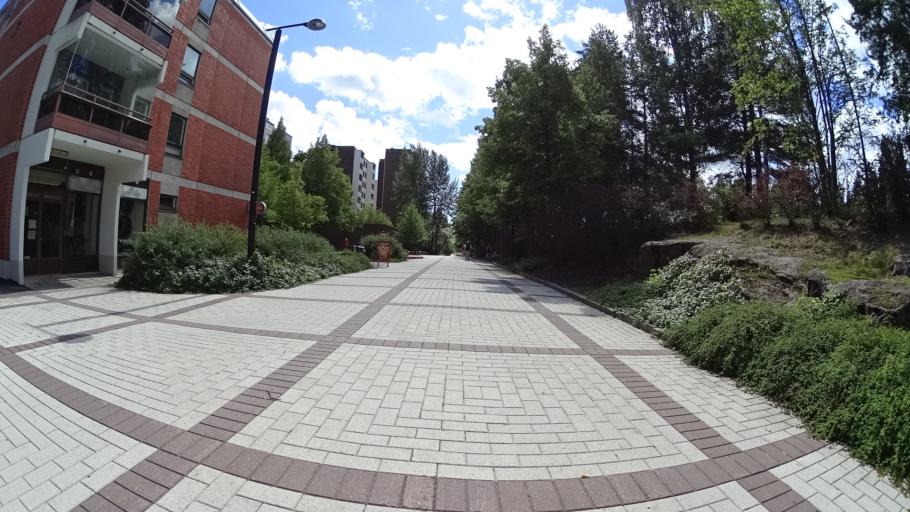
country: FI
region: Uusimaa
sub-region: Helsinki
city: Teekkarikylae
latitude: 60.2689
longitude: 24.8517
